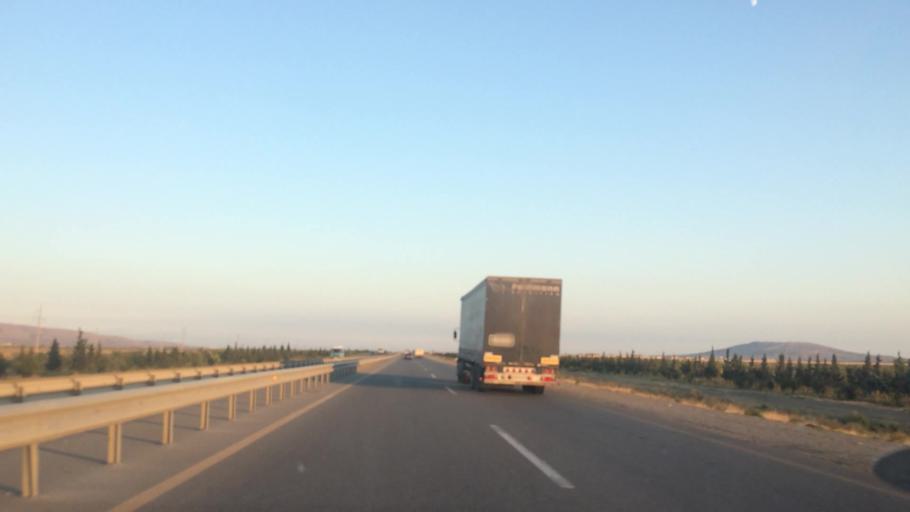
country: AZ
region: Baki
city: Qobustan
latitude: 39.9925
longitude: 49.1937
